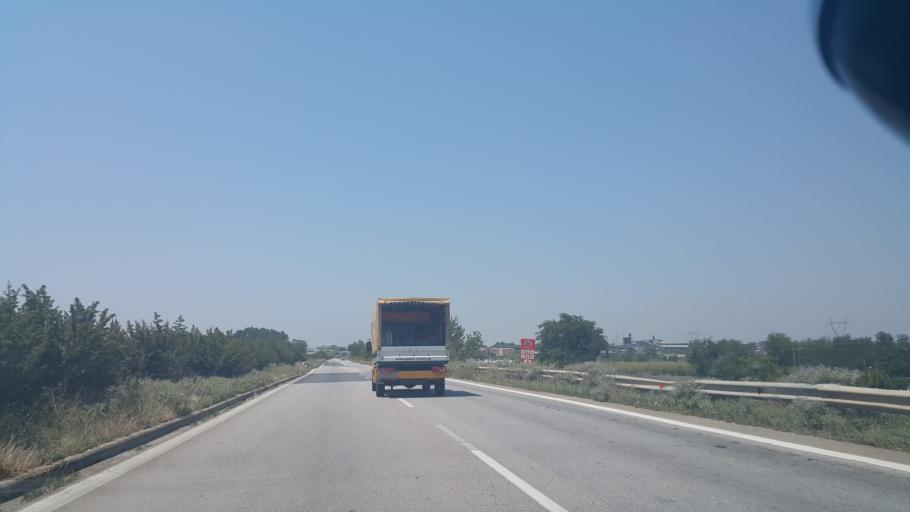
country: GR
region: Central Macedonia
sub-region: Nomos Thessalonikis
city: Nea Magnisia
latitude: 40.7002
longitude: 22.8354
